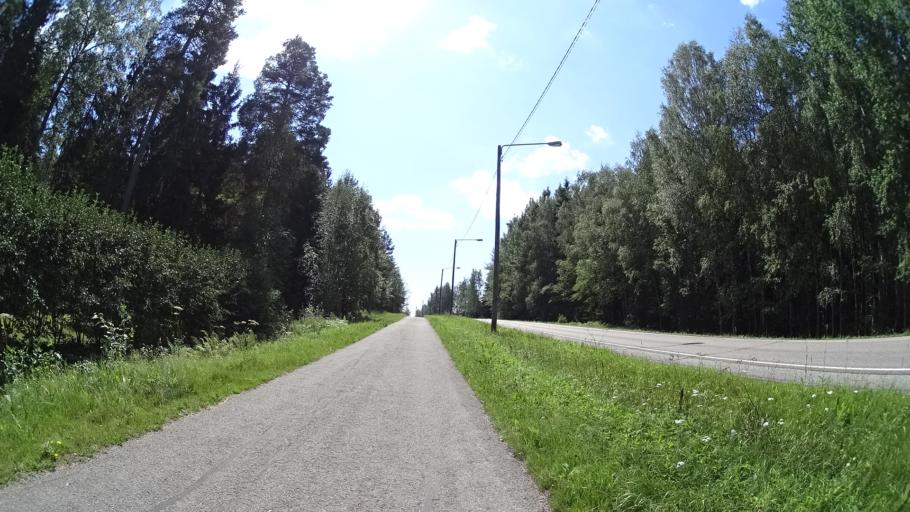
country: FI
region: Uusimaa
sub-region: Helsinki
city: Vantaa
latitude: 60.3279
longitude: 25.0020
